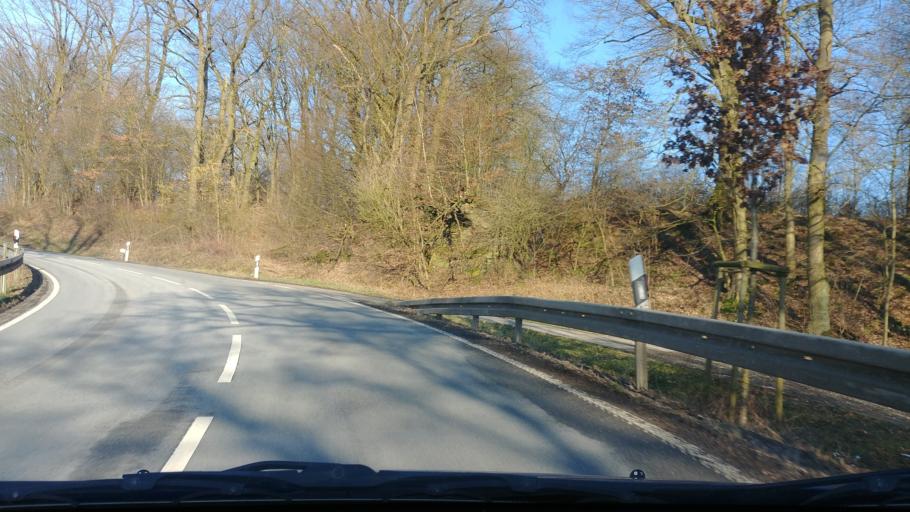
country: DE
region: Lower Saxony
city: Bad Karlshafen
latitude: 51.6146
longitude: 9.4331
